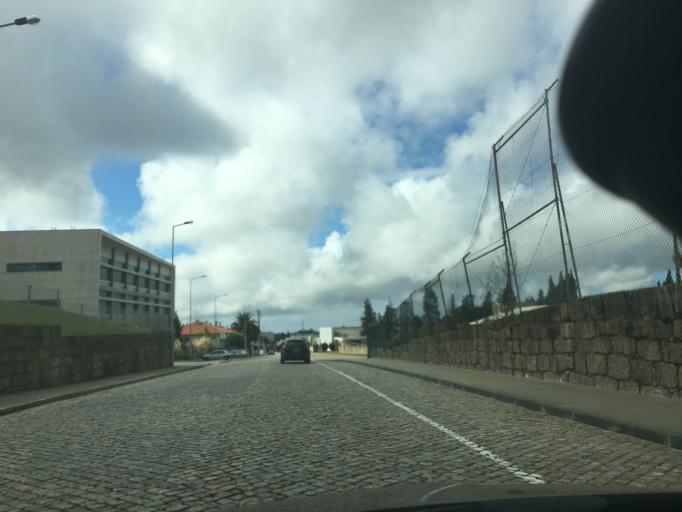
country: PT
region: Porto
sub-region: Maia
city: Gemunde
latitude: 41.2587
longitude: -8.6398
